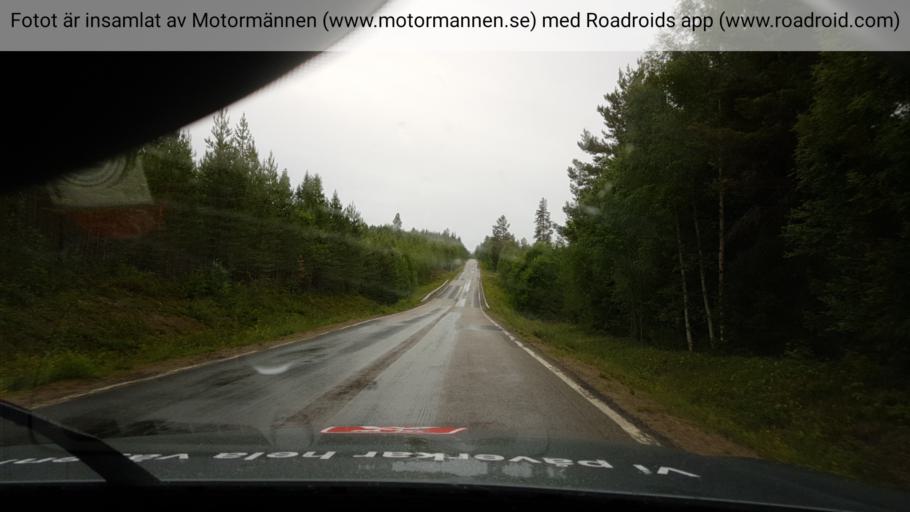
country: SE
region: Jaemtland
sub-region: Braecke Kommun
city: Braecke
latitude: 62.3369
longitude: 15.1312
